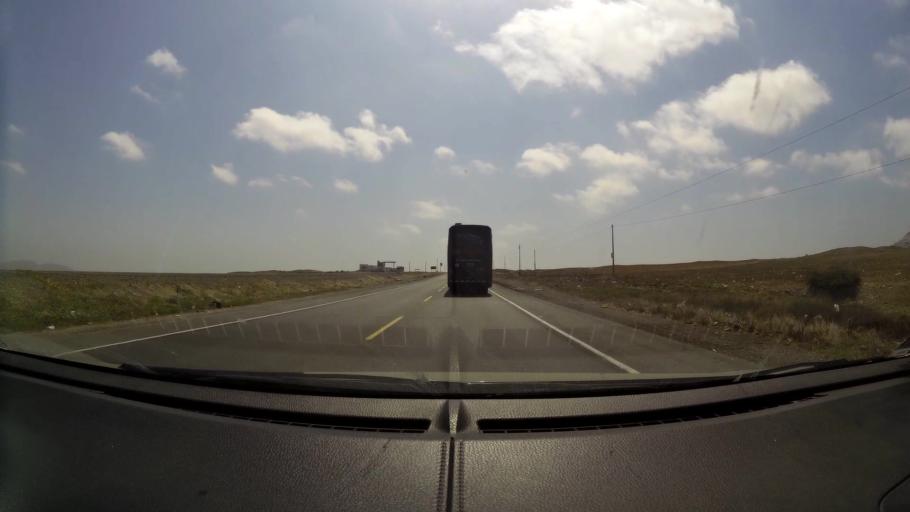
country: PE
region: Lambayeque
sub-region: Provincia de Chiclayo
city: Reque
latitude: -6.9047
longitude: -79.7783
